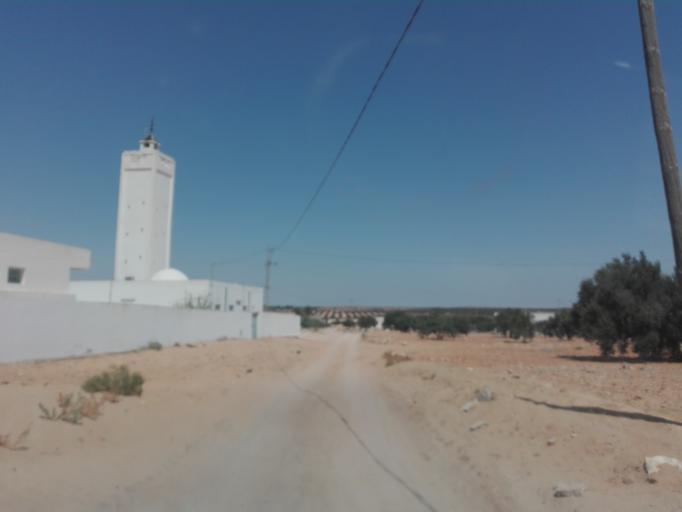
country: TN
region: Safaqis
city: Bi'r `Ali Bin Khalifah
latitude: 34.6478
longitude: 10.2553
